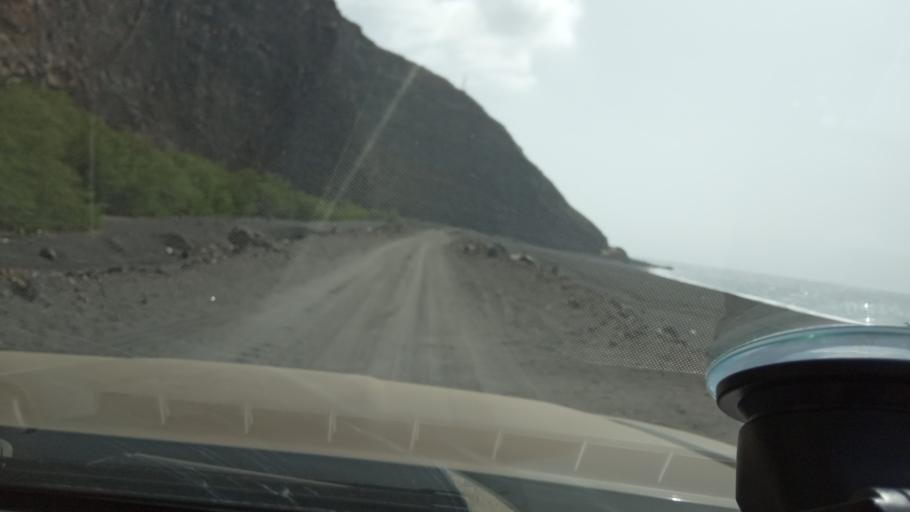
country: CV
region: Porto Novo
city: Porto Novo
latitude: 16.9496
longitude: -25.3098
